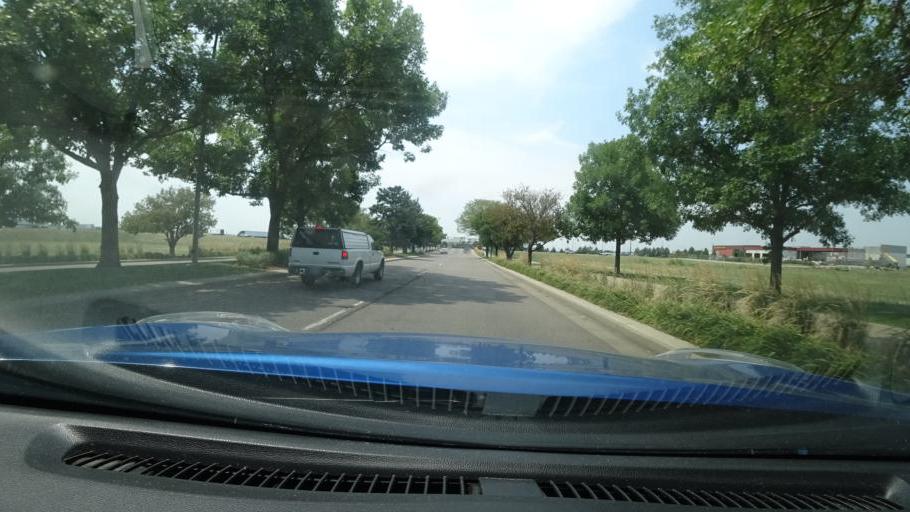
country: US
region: Colorado
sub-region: Adams County
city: Aurora
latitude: 39.7617
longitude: -104.7698
